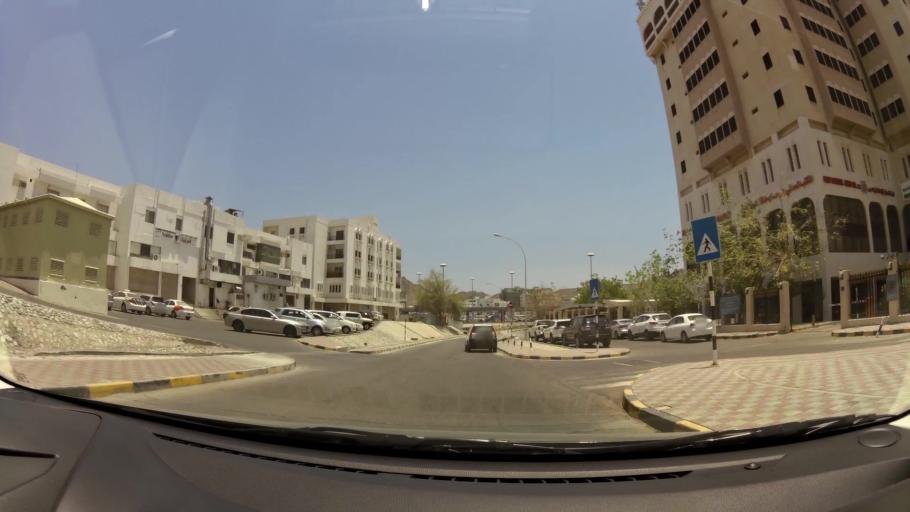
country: OM
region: Muhafazat Masqat
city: Muscat
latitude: 23.6126
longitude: 58.5434
